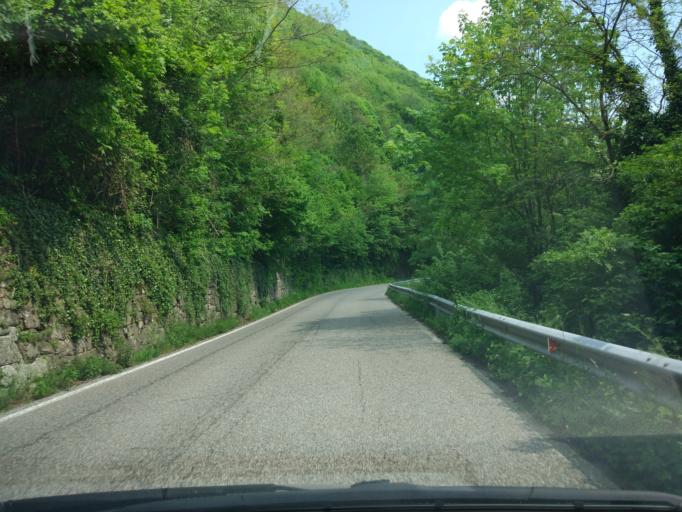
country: IT
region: Veneto
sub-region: Provincia di Verona
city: Selva di Progno
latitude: 45.6315
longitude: 11.1295
